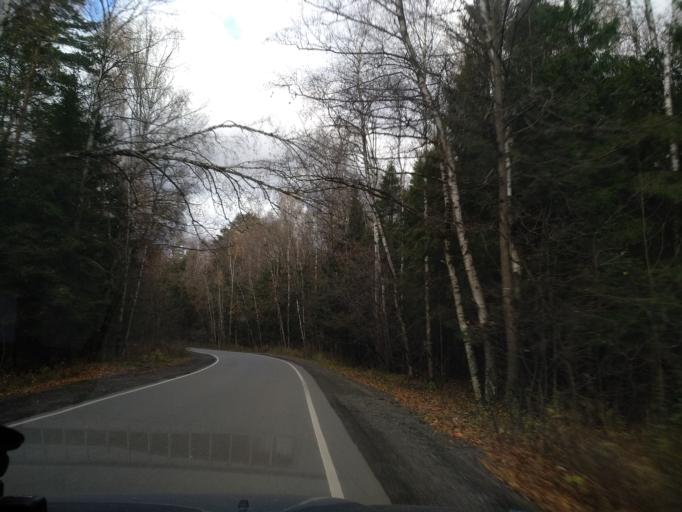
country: RU
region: Moscow
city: Lianozovo
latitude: 55.9134
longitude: 37.6094
